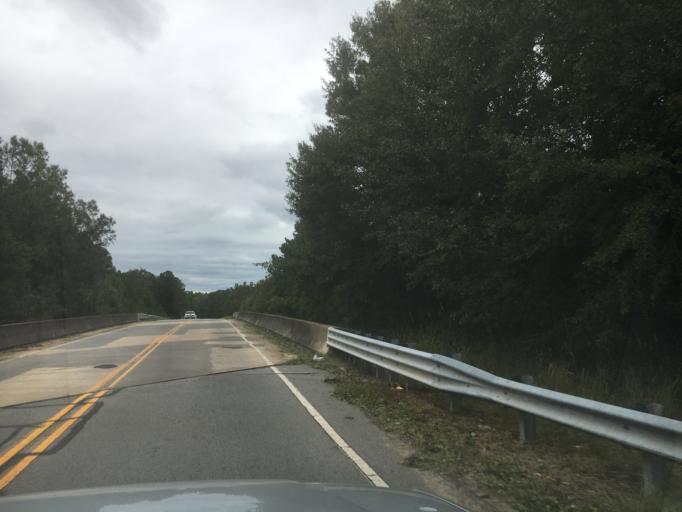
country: US
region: South Carolina
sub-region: McCormick County
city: McCormick
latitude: 34.0540
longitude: -82.2412
